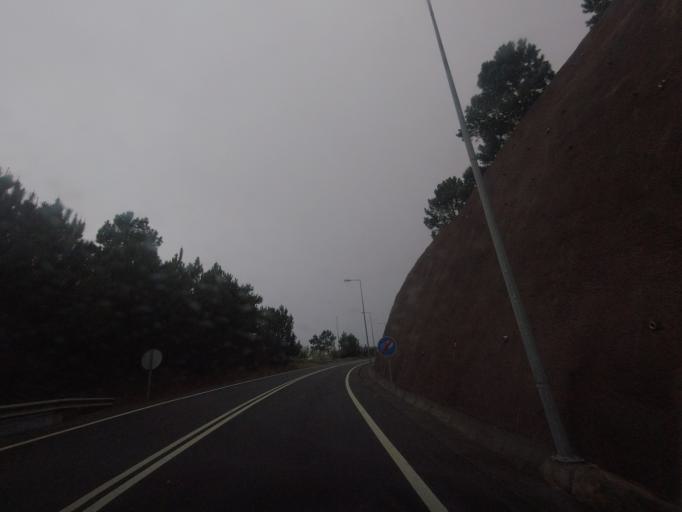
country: PT
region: Madeira
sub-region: Calheta
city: Estreito da Calheta
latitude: 32.7474
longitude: -17.2109
